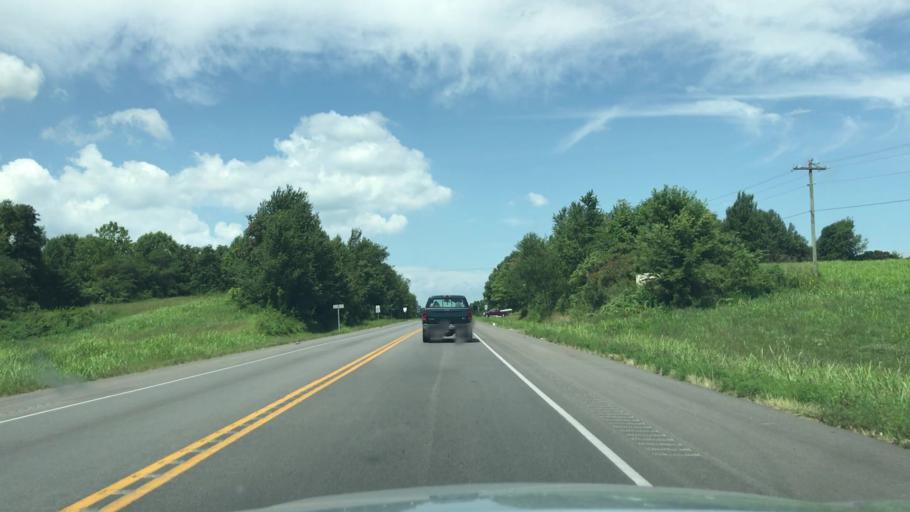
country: US
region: Kentucky
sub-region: Clinton County
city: Albany
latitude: 36.7535
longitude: -85.1204
